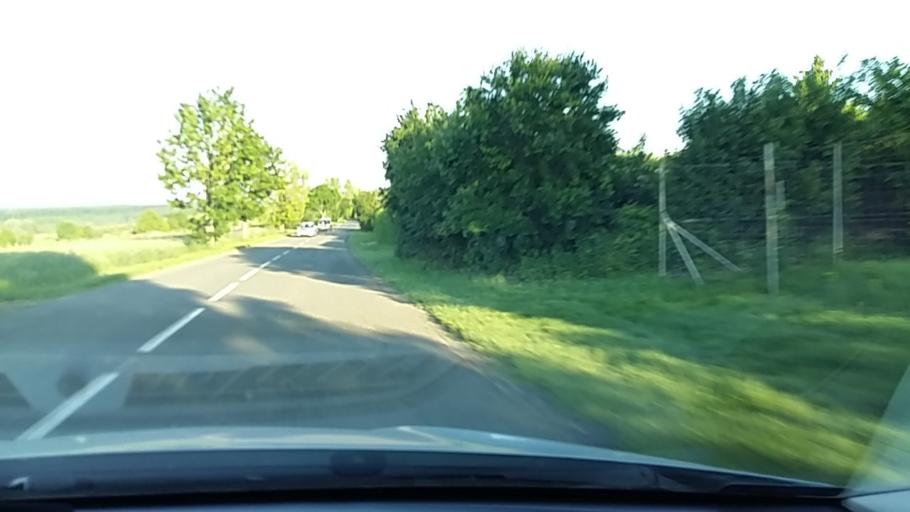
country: HU
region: Nograd
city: Diosjeno
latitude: 47.9042
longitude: 19.0704
